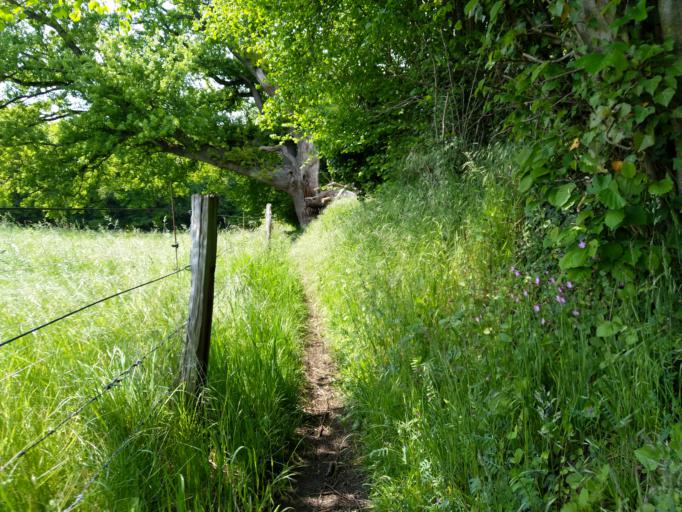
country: BE
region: Wallonia
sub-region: Province du Hainaut
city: Estinnes-au-Val
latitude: 50.4613
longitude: 4.0383
